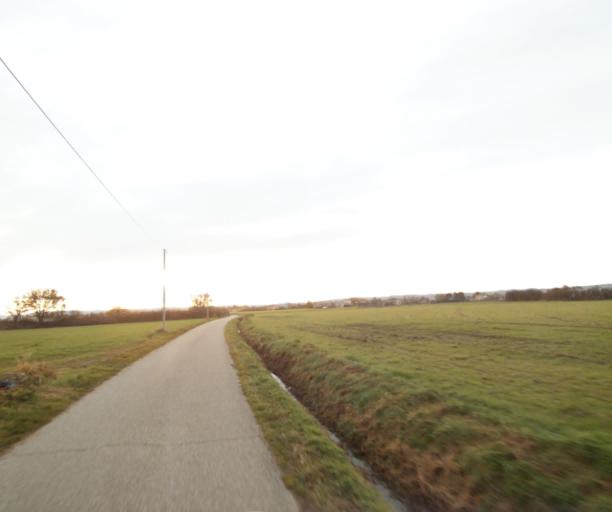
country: FR
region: Rhone-Alpes
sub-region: Departement de la Loire
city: Sury-le-Comtal
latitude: 45.5457
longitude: 4.1655
